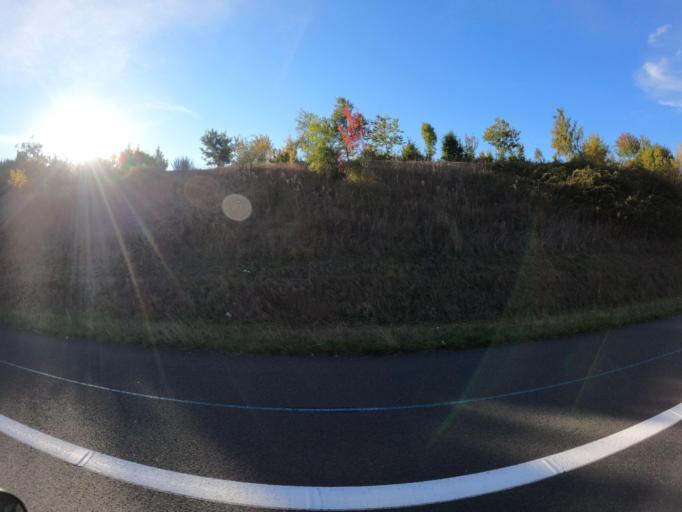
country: FR
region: Pays de la Loire
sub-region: Departement de Maine-et-Loire
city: Chemille-Melay
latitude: 47.2197
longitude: -0.7612
